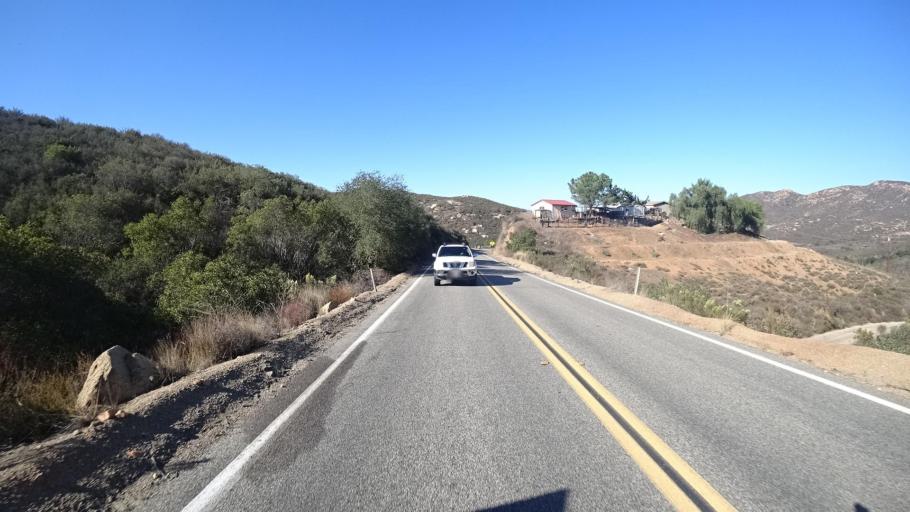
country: US
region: California
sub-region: San Diego County
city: Jamul
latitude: 32.6727
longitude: -116.7743
